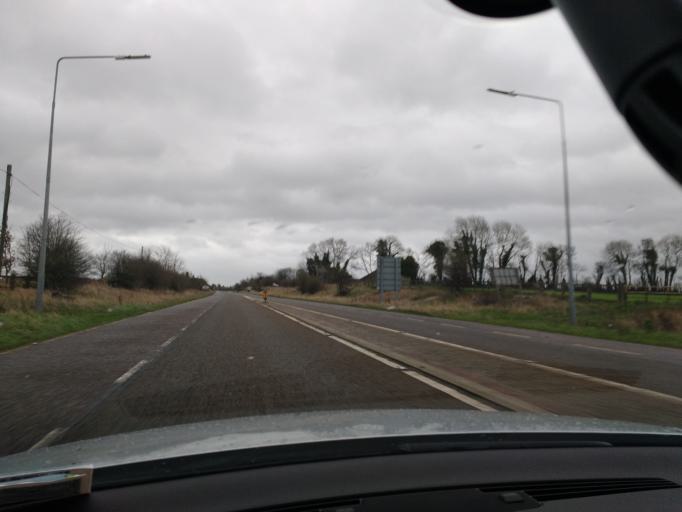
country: IE
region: Munster
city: Thurles
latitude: 52.6707
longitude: -7.6823
